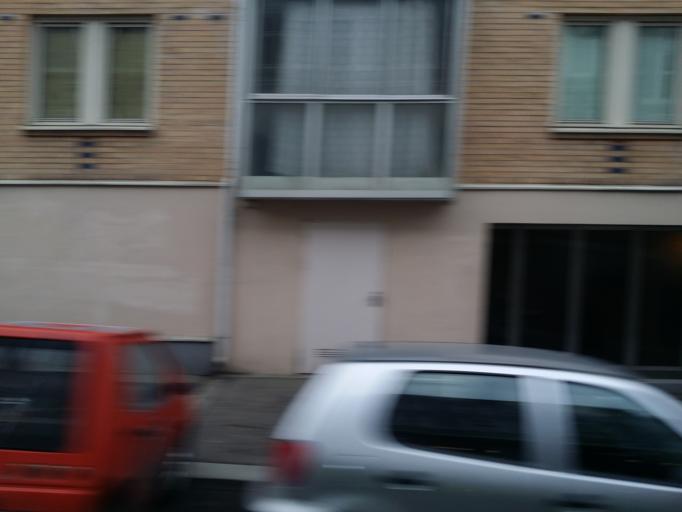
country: NO
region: Oslo
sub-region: Oslo
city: Oslo
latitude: 59.9078
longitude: 10.7711
